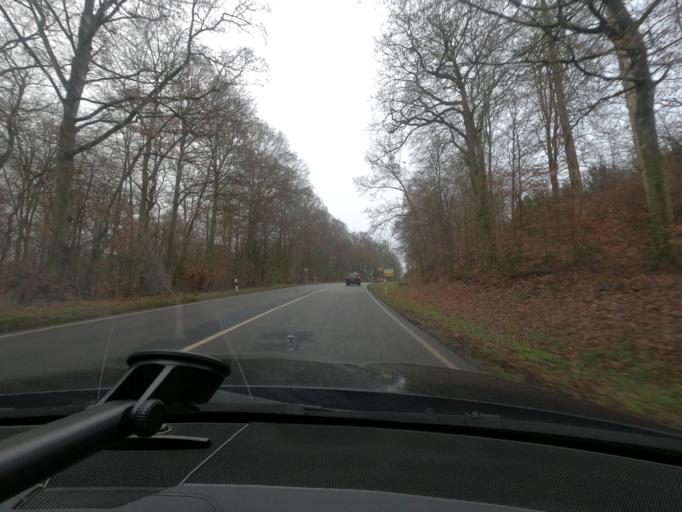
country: DE
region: Hesse
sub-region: Regierungsbezirk Kassel
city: Bad Arolsen
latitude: 51.3712
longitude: 9.0480
